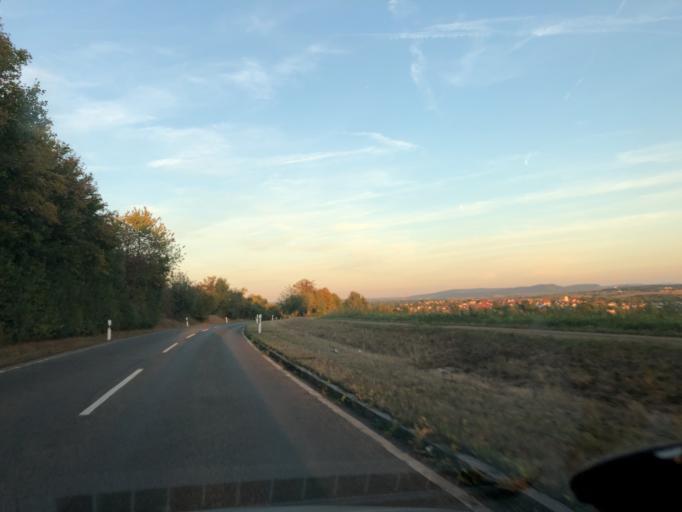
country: DE
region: Baden-Wuerttemberg
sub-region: Regierungsbezirk Stuttgart
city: Marbach am Neckar
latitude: 48.9178
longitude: 9.2462
